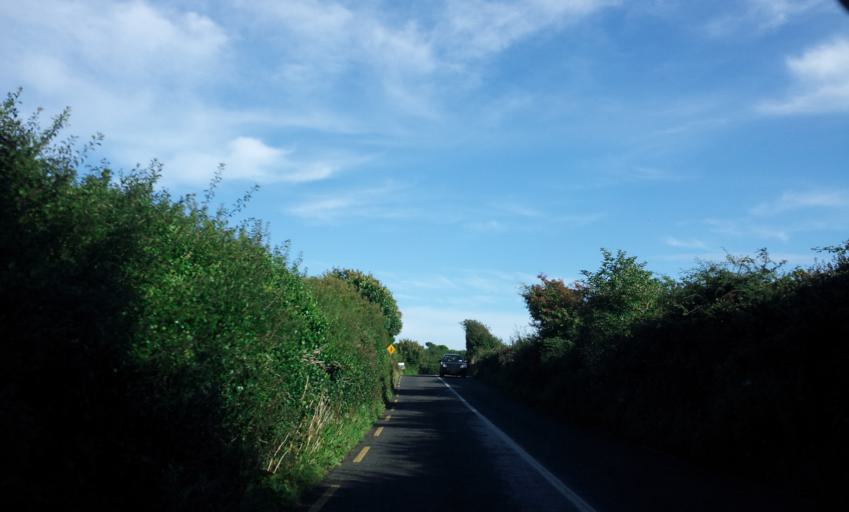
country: IE
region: Munster
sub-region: An Clar
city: Ennis
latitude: 52.9759
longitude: -9.1004
